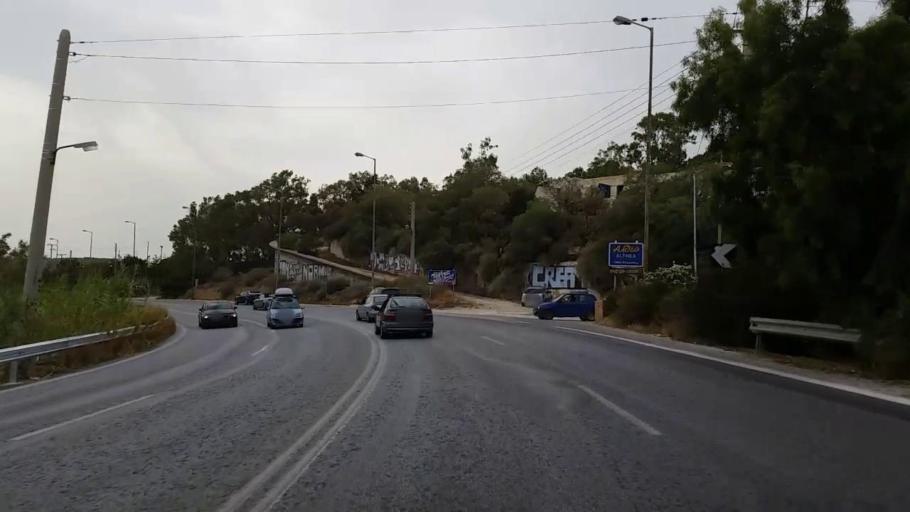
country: GR
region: Attica
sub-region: Nomarchia Anatolikis Attikis
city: Agios Dimitrios Kropias
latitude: 37.8061
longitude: 23.8528
